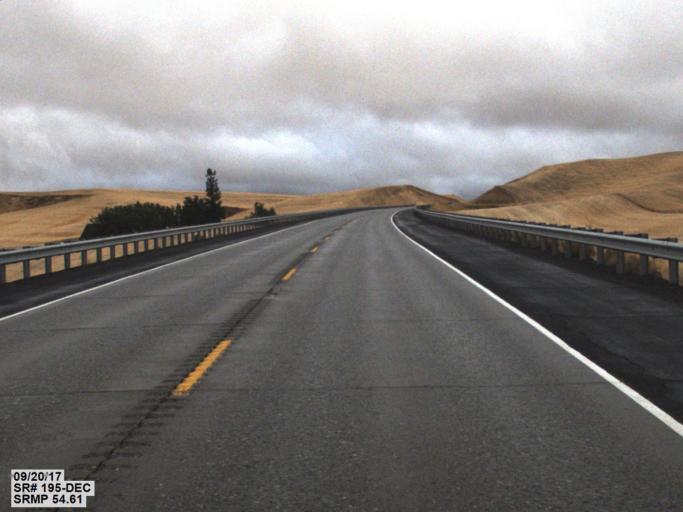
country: US
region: Washington
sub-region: Whitman County
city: Colfax
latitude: 47.0970
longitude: -117.3789
